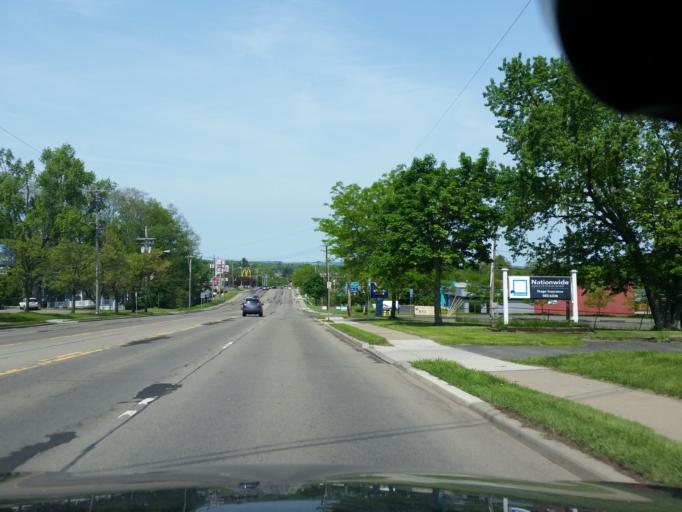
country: US
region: New York
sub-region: Chautauqua County
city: Jamestown West
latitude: 42.0974
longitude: -79.2864
